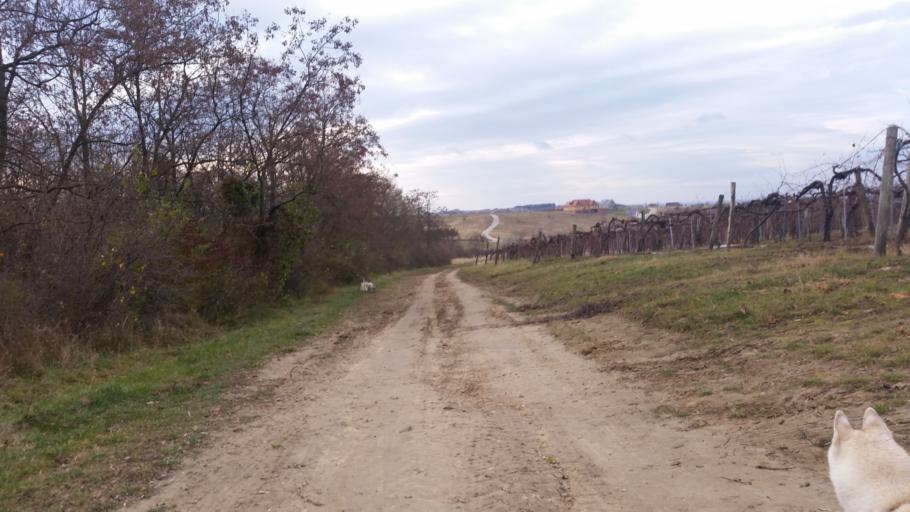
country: HU
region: Pest
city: Telki
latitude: 47.5673
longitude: 18.8116
